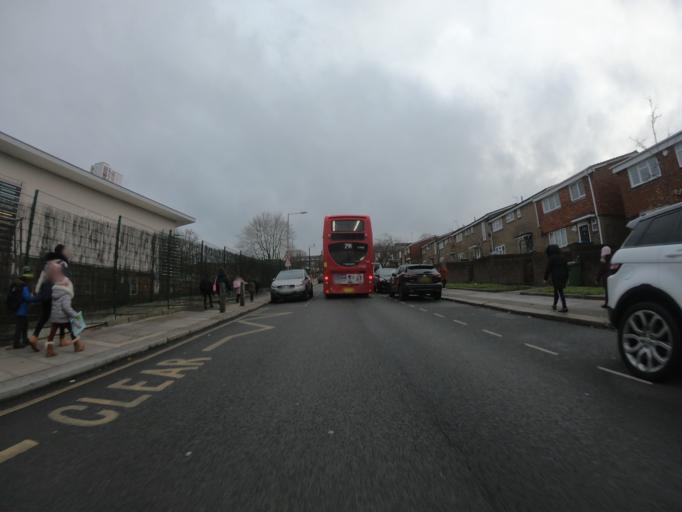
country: GB
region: England
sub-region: Greater London
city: Woolwich
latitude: 51.4870
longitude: 0.0735
